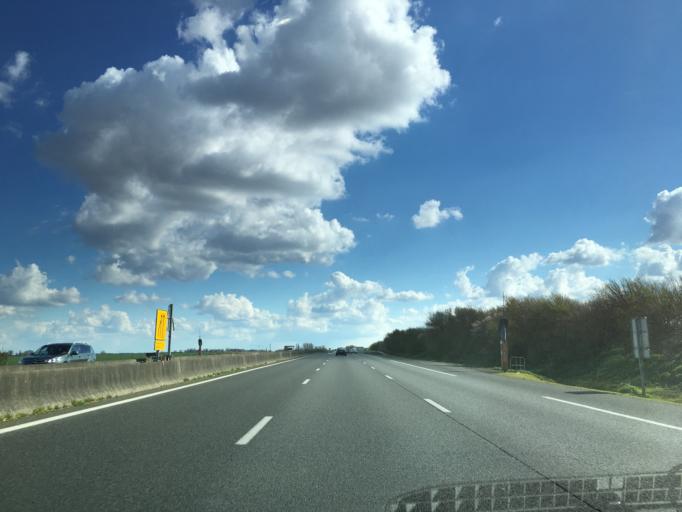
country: FR
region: Nord-Pas-de-Calais
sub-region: Departement du Pas-de-Calais
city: Bapaume
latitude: 50.1172
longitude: 2.8714
